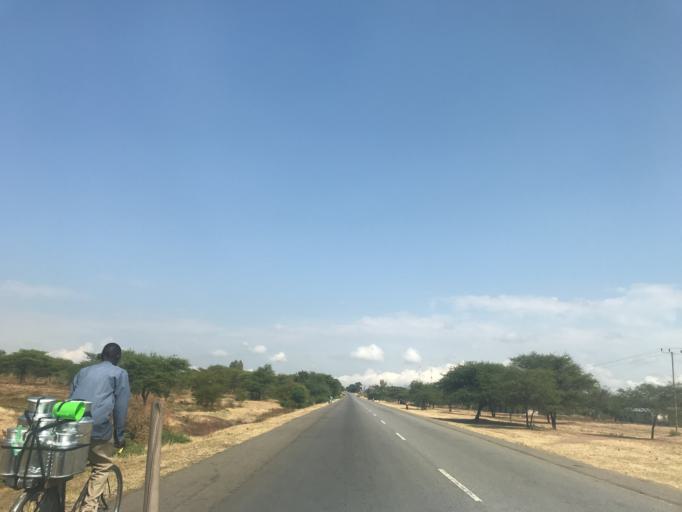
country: TZ
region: Mwanza
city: Nyanguge
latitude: -2.5400
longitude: 33.1859
